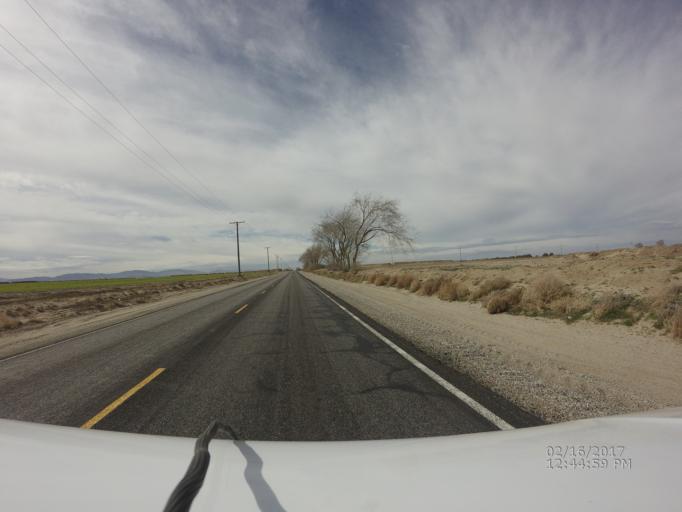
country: US
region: California
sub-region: Los Angeles County
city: Lake Los Angeles
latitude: 34.6754
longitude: -117.9409
